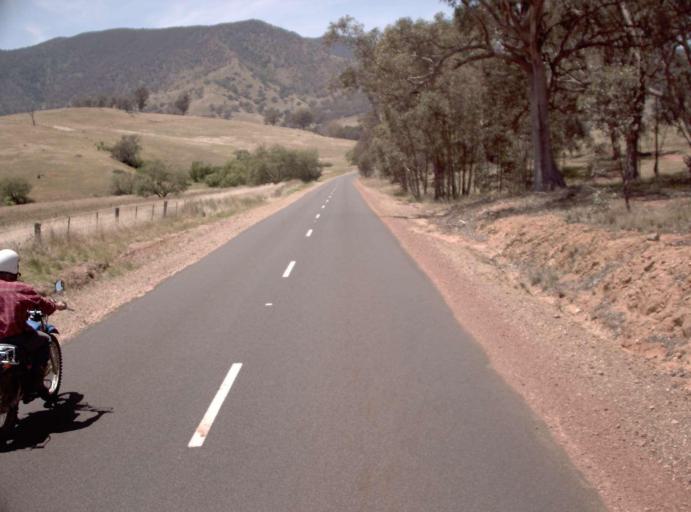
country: AU
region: Victoria
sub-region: East Gippsland
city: Bairnsdale
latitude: -37.1836
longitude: 147.7134
